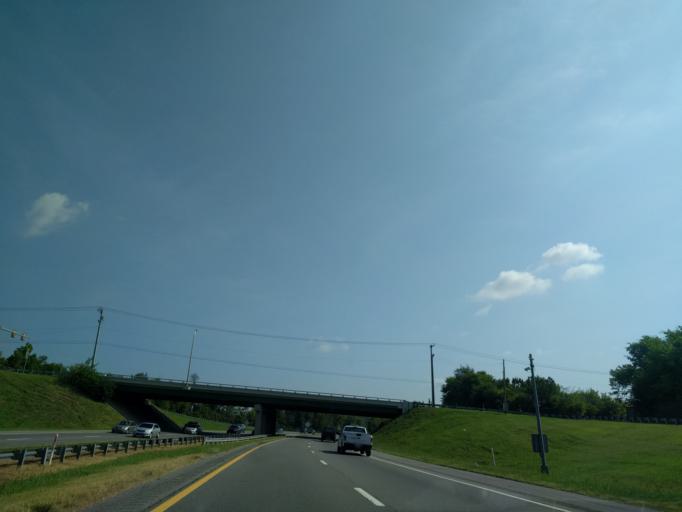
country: US
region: Tennessee
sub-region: Davidson County
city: Nashville
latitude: 36.1842
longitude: -86.7602
